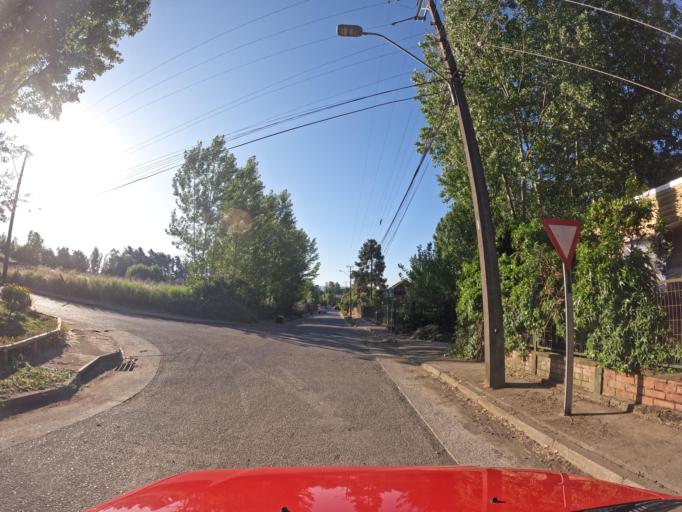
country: CL
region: Biobio
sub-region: Provincia de Concepcion
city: Lota
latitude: -37.1716
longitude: -72.9388
